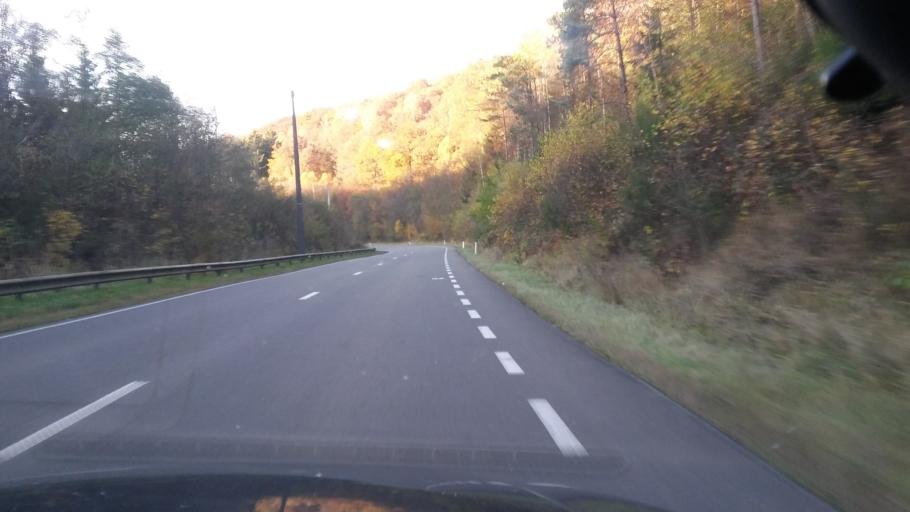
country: BE
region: Wallonia
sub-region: Province du Luxembourg
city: Bouillon
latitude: 49.7622
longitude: 5.0955
